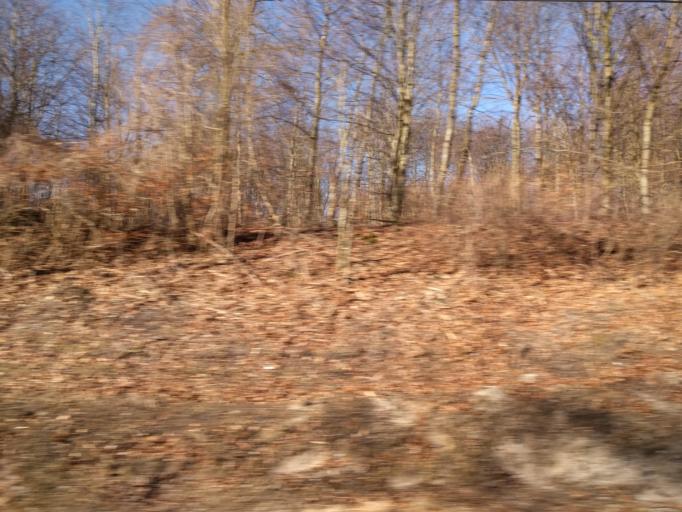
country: DK
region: Capital Region
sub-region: Rudersdal Kommune
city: Trorod
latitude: 55.8304
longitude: 12.5692
